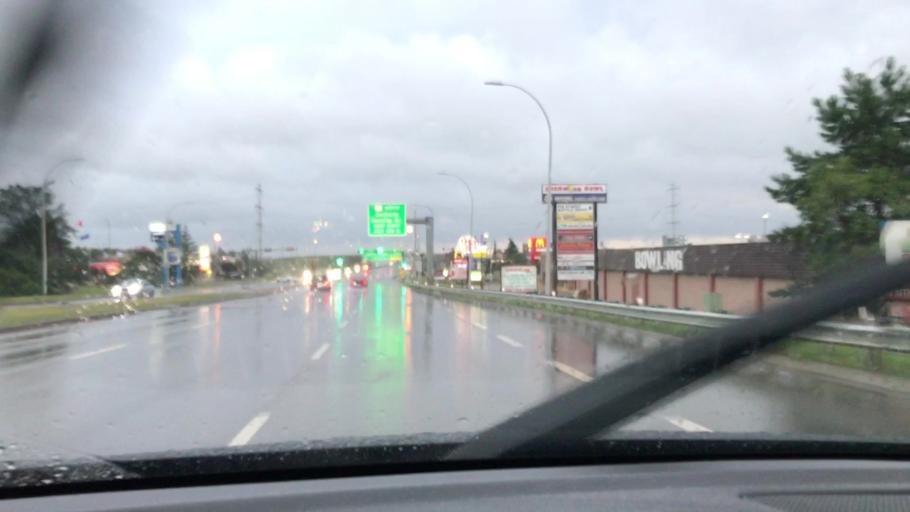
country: CA
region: Alberta
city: Sherwood Park
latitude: 53.5122
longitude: -113.3276
